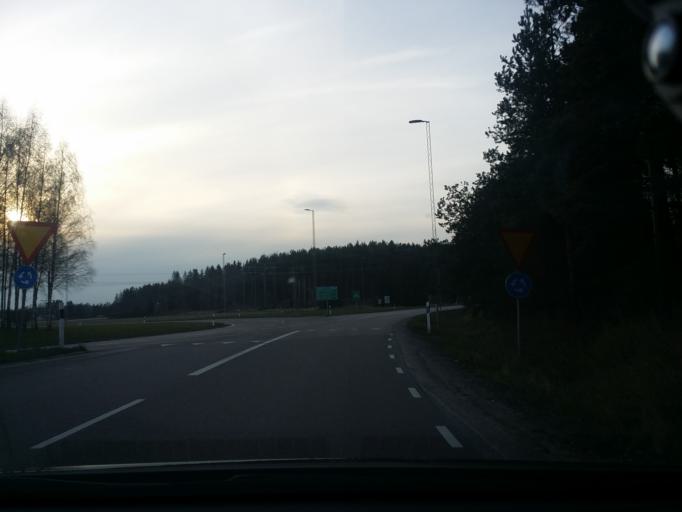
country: SE
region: Uppsala
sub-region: Enkopings Kommun
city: Enkoping
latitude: 59.6386
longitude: 17.0565
